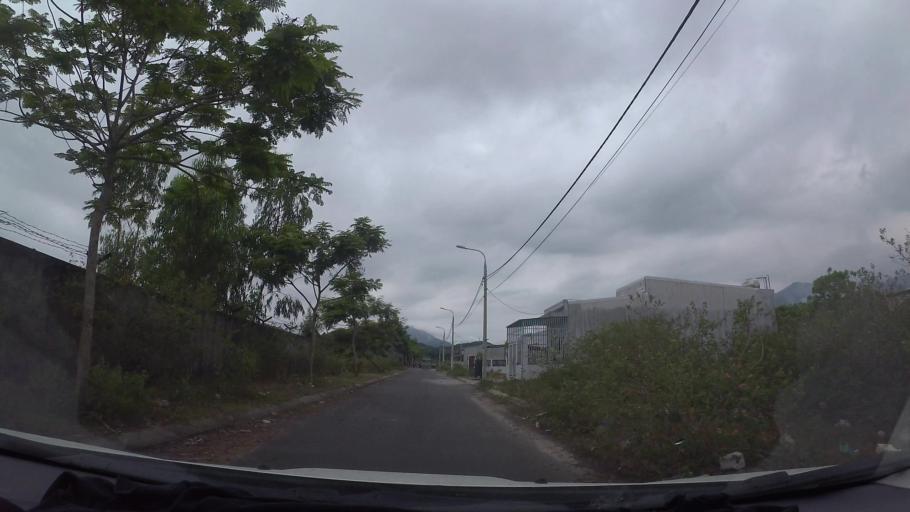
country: VN
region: Da Nang
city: Lien Chieu
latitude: 16.1245
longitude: 108.1166
